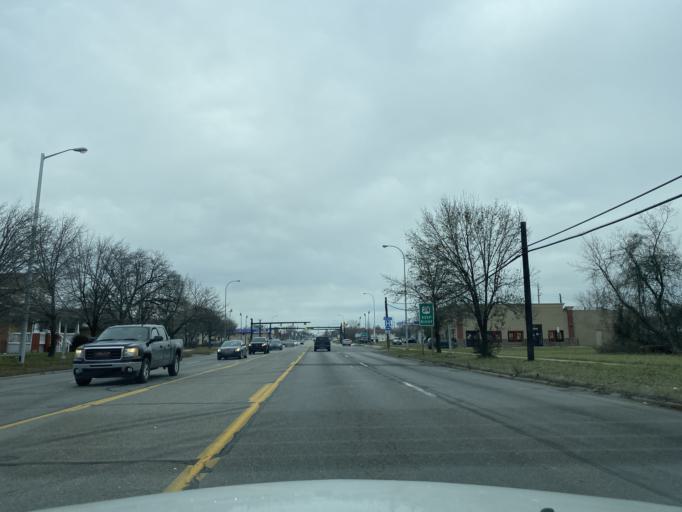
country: US
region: Michigan
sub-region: Wayne County
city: Taylor
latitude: 42.1975
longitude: -83.2701
